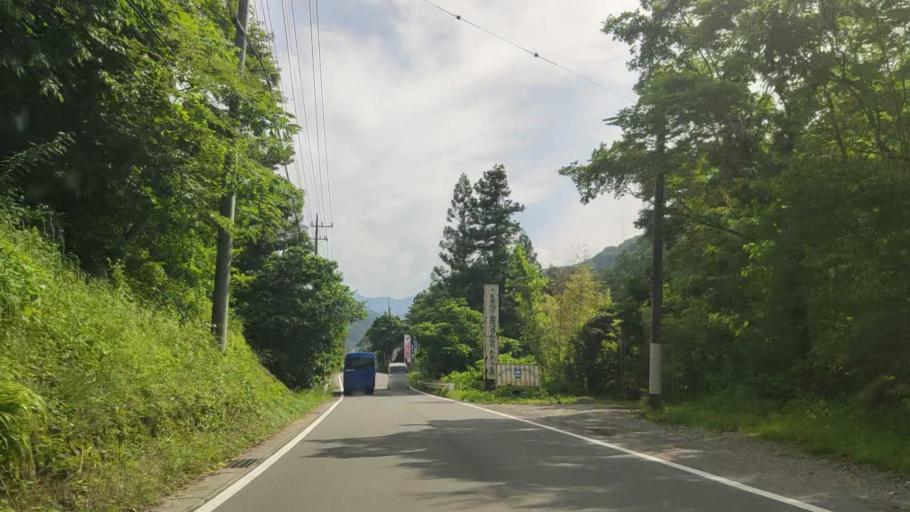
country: JP
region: Gunma
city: Tomioka
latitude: 36.1939
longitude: 138.7535
